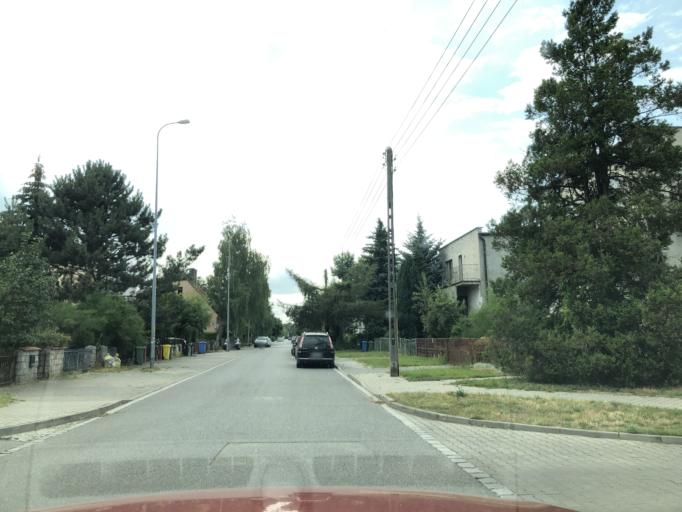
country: PL
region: Lower Silesian Voivodeship
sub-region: Powiat wroclawski
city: Smolec
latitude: 51.1564
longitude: 16.9042
